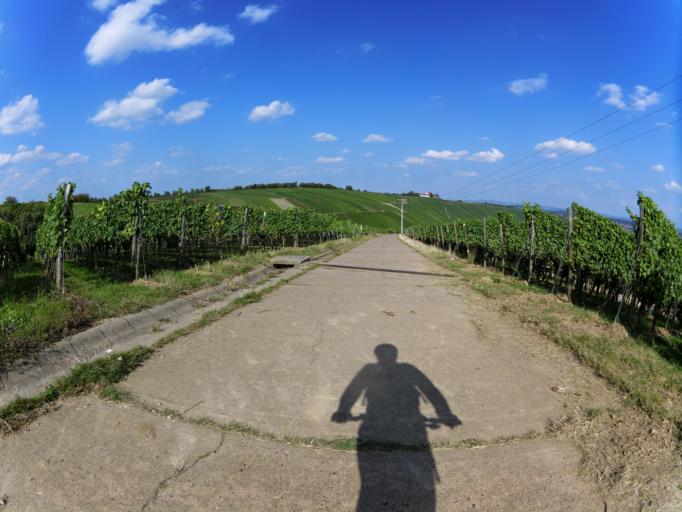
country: DE
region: Bavaria
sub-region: Regierungsbezirk Unterfranken
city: Nordheim
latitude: 49.8611
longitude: 10.1694
